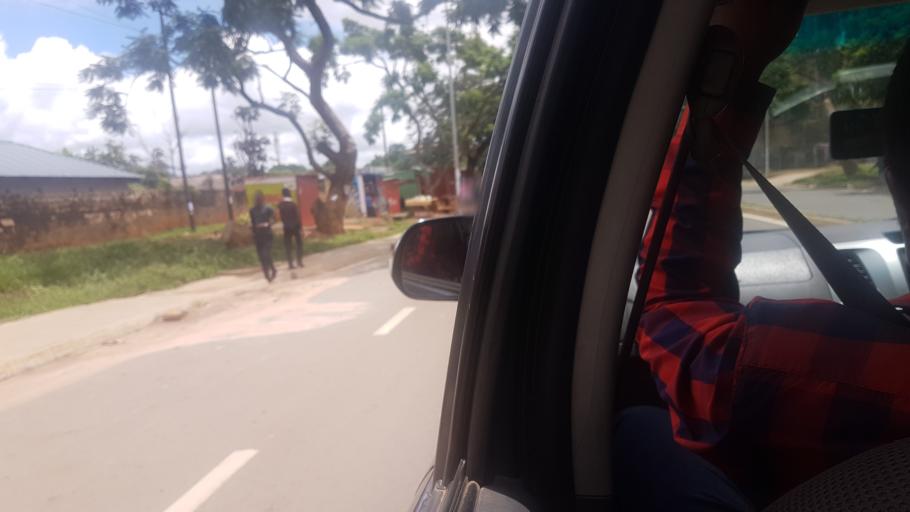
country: ZM
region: Lusaka
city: Lusaka
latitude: -15.4341
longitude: 28.3121
